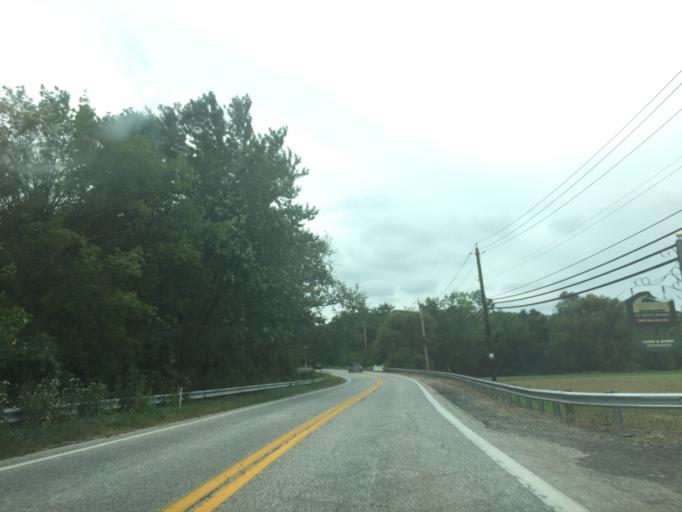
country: US
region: Maryland
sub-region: Baltimore County
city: Kingsville
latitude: 39.4635
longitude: -76.4651
